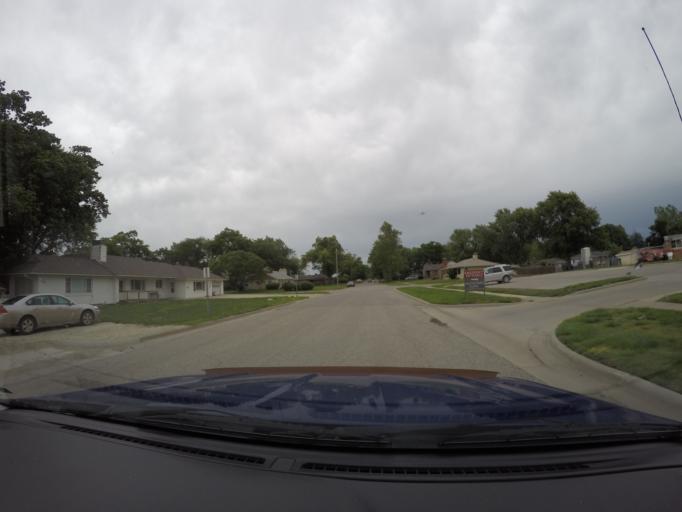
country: US
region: Kansas
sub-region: Clay County
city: Clay Center
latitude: 39.3922
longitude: -97.1245
